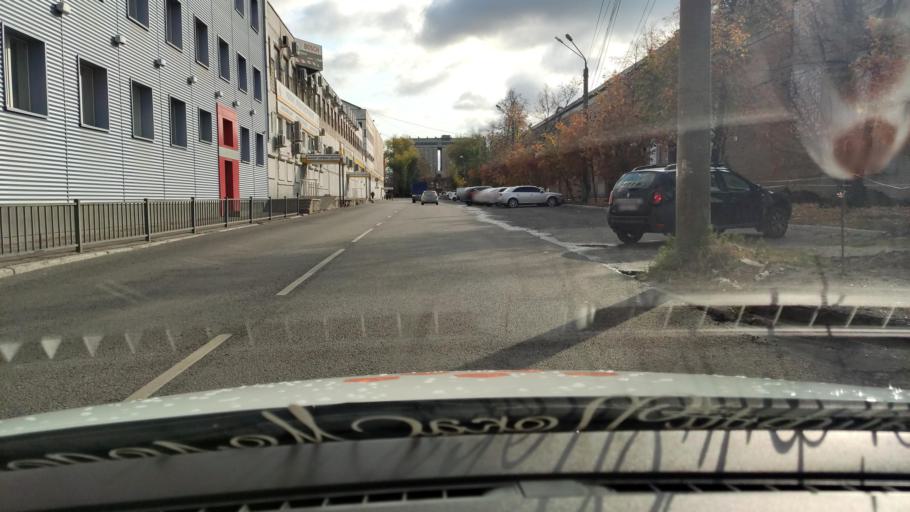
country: RU
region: Voronezj
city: Voronezh
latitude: 51.6806
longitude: 39.1725
